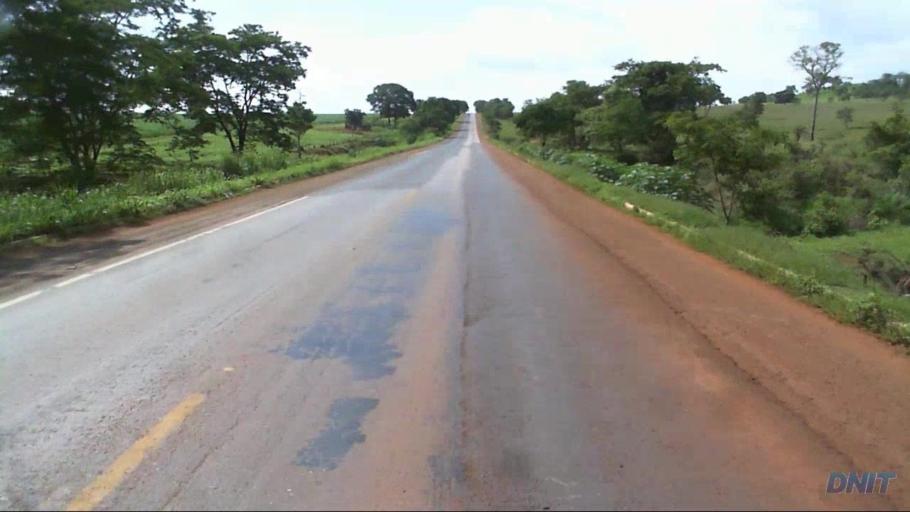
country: BR
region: Goias
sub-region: Barro Alto
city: Barro Alto
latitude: -15.0133
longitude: -48.9001
